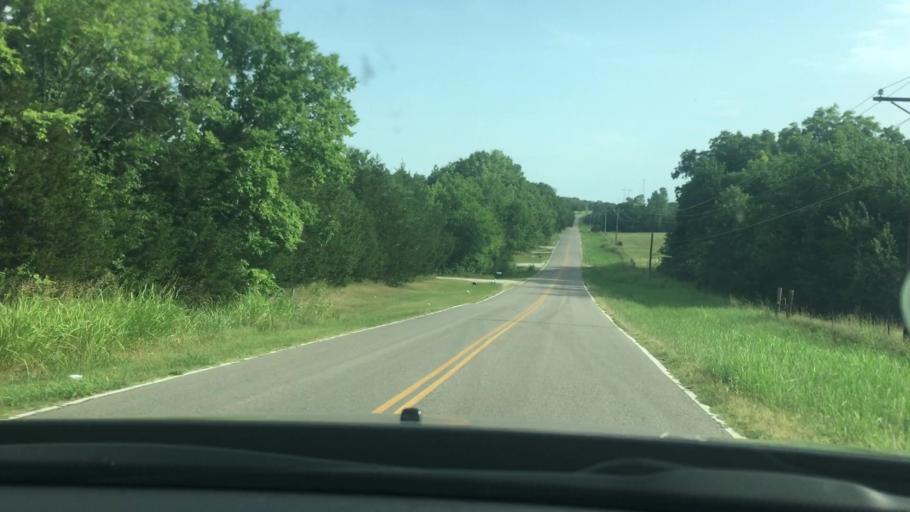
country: US
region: Oklahoma
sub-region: Pontotoc County
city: Byng
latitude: 34.8572
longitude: -96.6135
